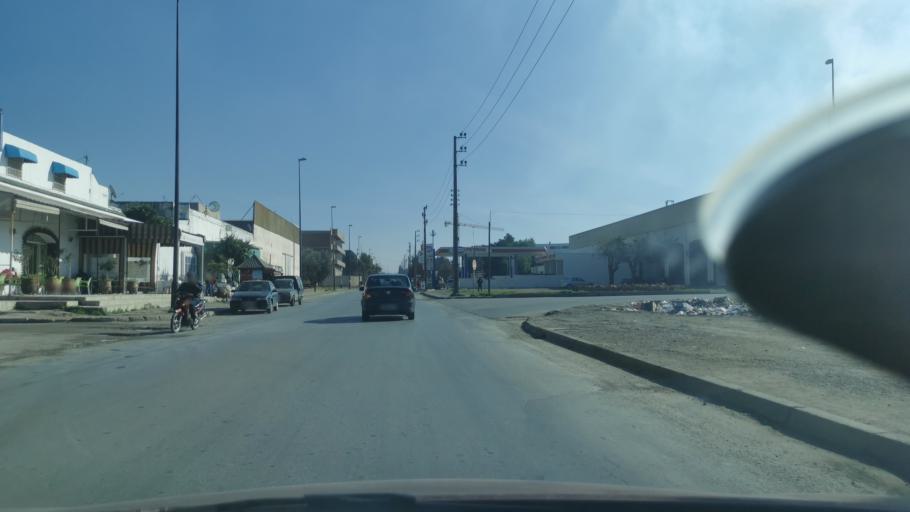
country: MA
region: Fes-Boulemane
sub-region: Fes
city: Fes
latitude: 34.0297
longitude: -4.9825
